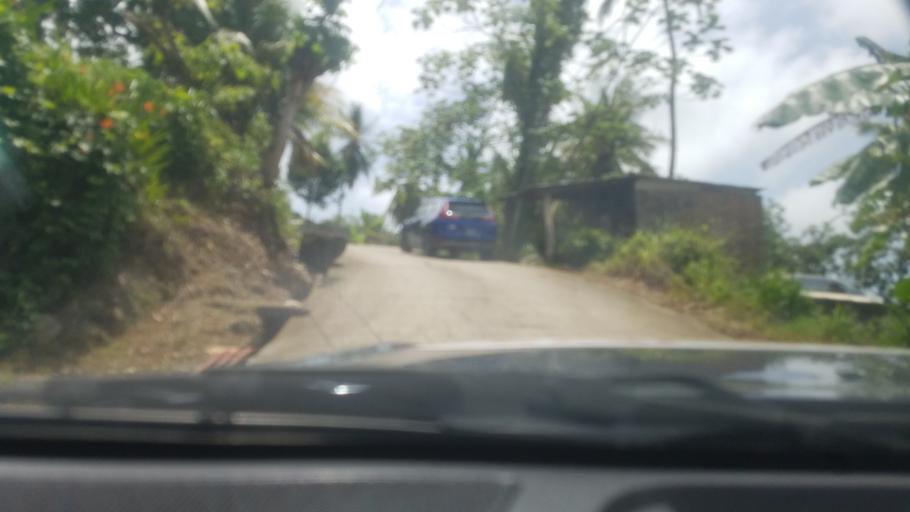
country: LC
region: Micoud Quarter
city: Micoud
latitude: 13.8015
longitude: -60.9497
